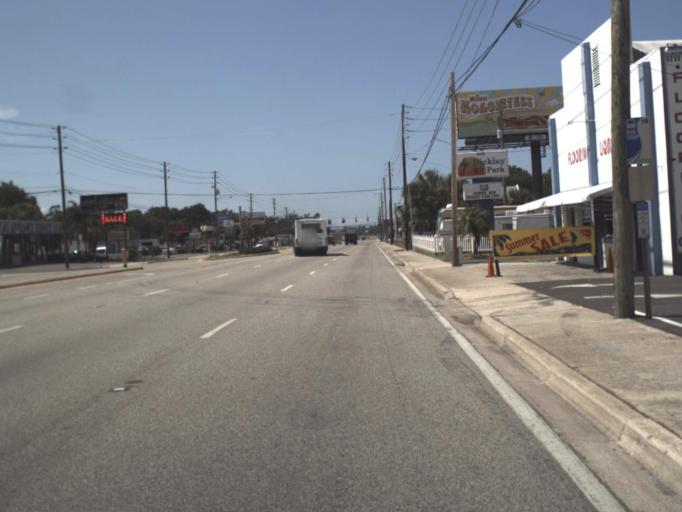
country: US
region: Florida
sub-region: Pinellas County
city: Bay Pines
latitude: 27.8237
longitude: -82.7871
